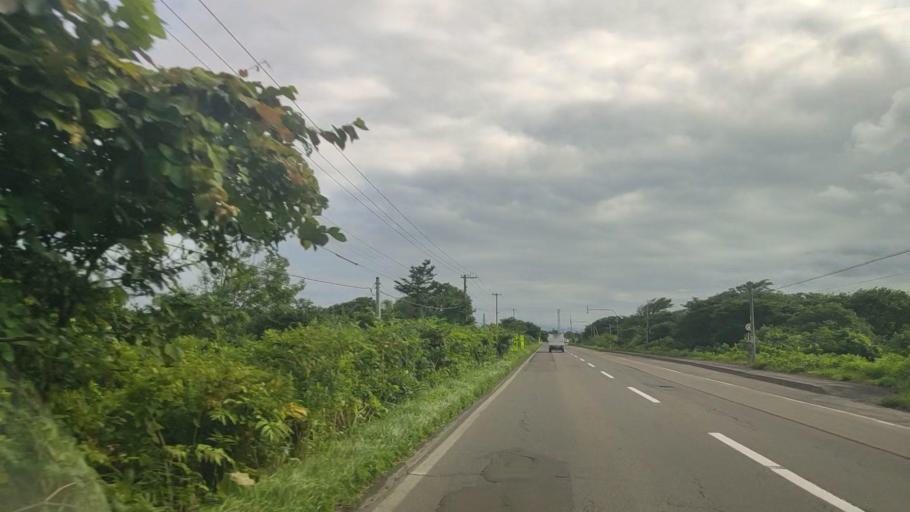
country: JP
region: Hokkaido
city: Niseko Town
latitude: 42.4634
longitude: 140.3383
